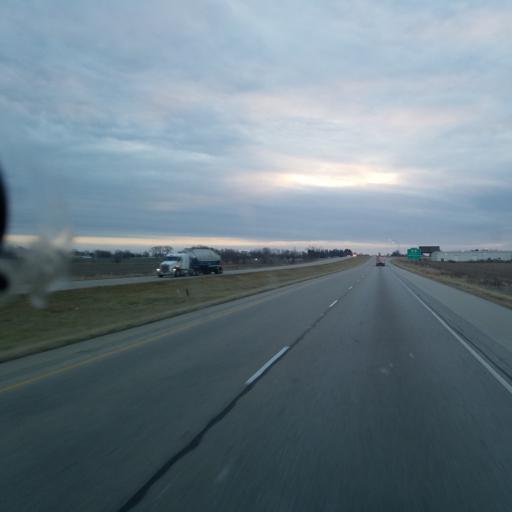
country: US
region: Illinois
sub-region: McLean County
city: Bloomington
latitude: 40.4361
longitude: -88.9998
